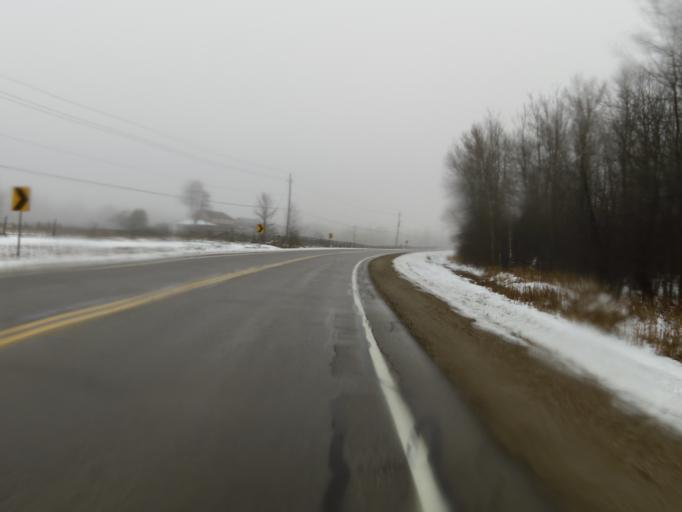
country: CA
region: Ontario
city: Perth
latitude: 44.8281
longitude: -76.3913
